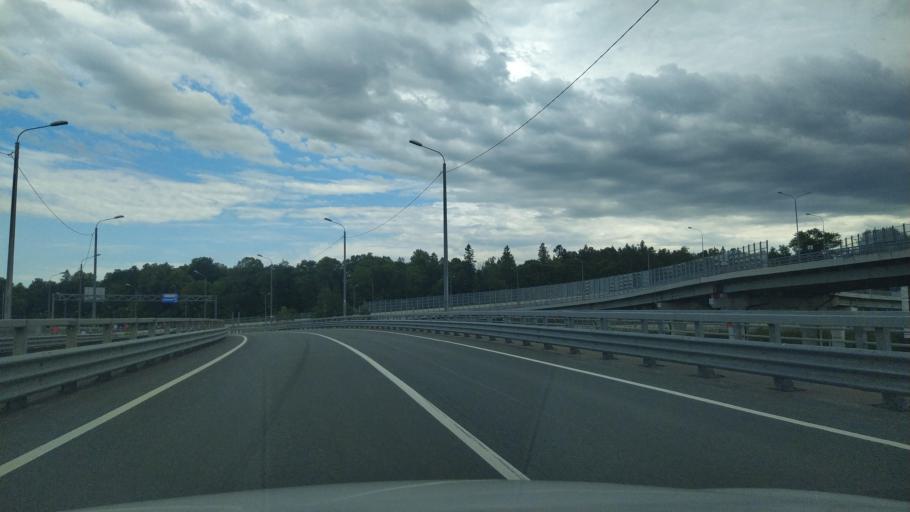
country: RU
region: St.-Petersburg
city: Bol'shaya Izhora
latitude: 59.9285
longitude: 29.6726
